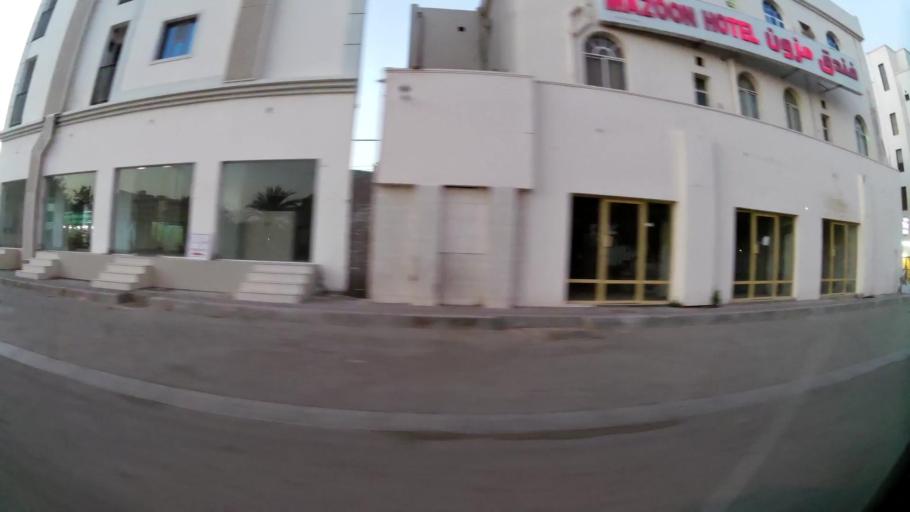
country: OM
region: Muhafazat Masqat
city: As Sib al Jadidah
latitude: 23.6823
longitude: 58.1805
